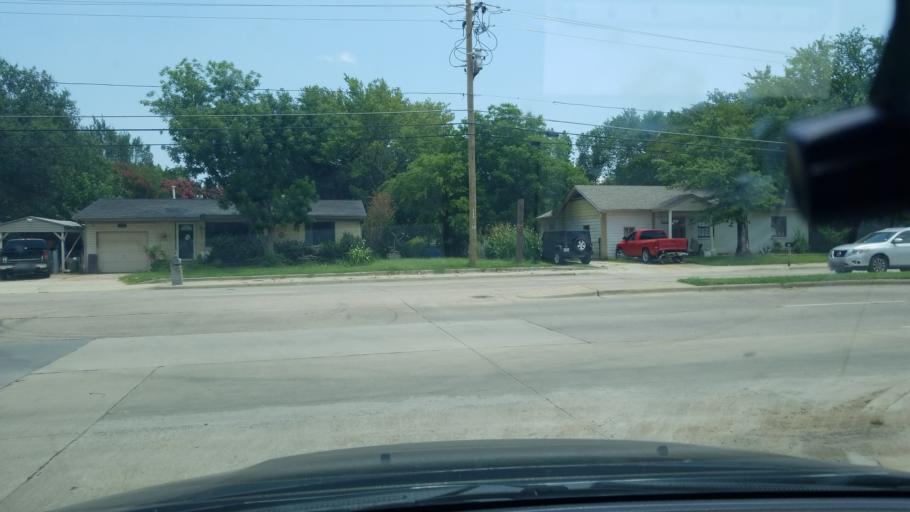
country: US
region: Texas
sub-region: Dallas County
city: Balch Springs
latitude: 32.7149
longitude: -96.6487
